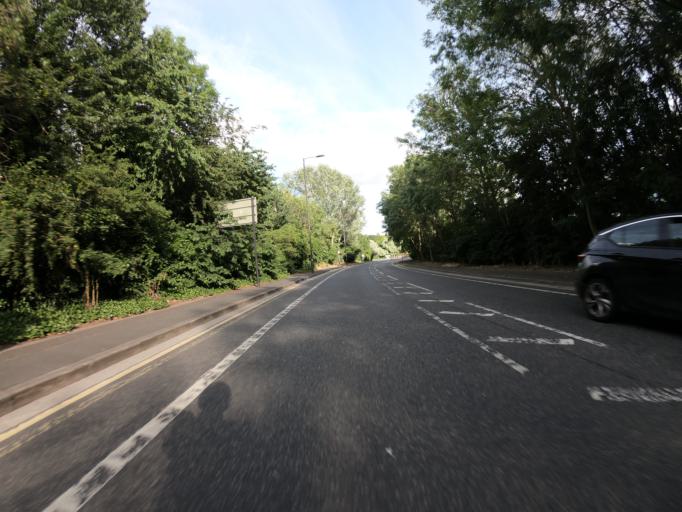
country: GB
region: England
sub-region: Greater London
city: Woolwich
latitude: 51.5118
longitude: 0.0671
